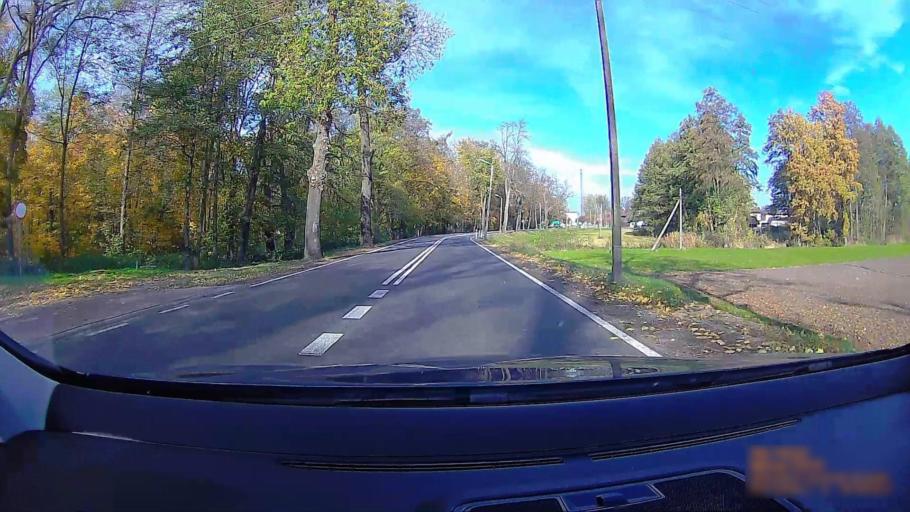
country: PL
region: Greater Poland Voivodeship
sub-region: Powiat ostrzeszowski
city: Doruchow
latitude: 51.4139
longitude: 18.0760
